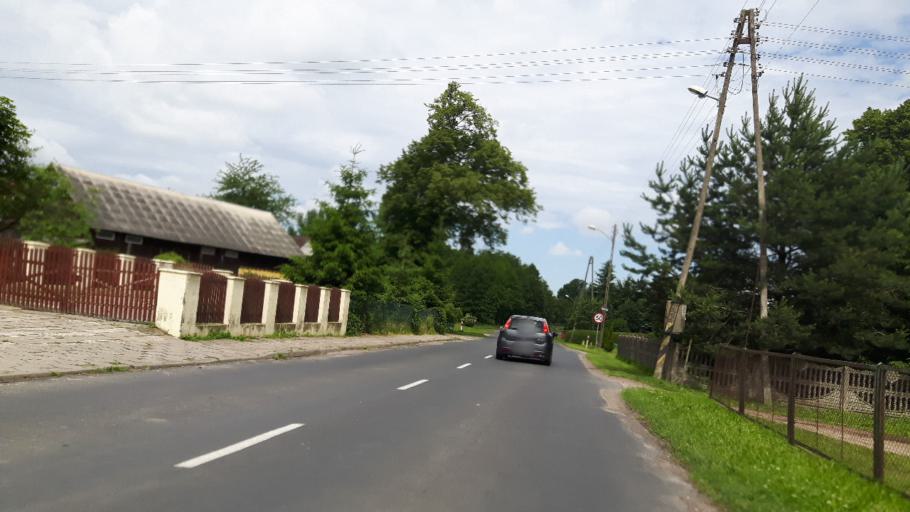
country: PL
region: West Pomeranian Voivodeship
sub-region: Powiat gryficki
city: Trzebiatow
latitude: 54.0131
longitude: 15.2452
